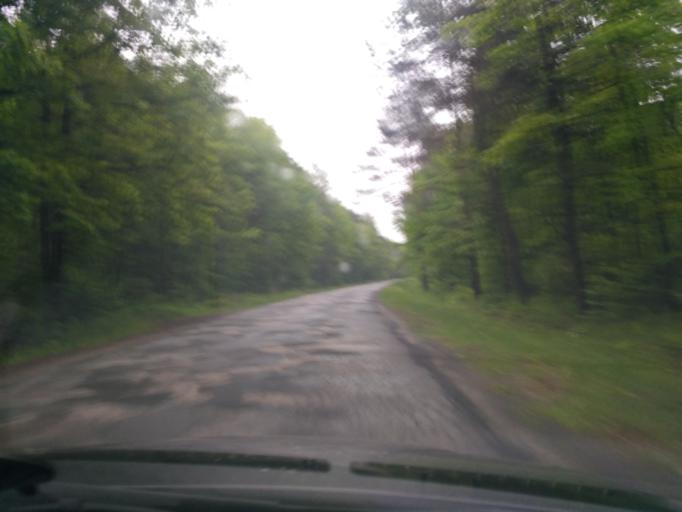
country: PL
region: Subcarpathian Voivodeship
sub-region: Powiat debicki
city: Pilzno
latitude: 49.9759
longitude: 21.3632
